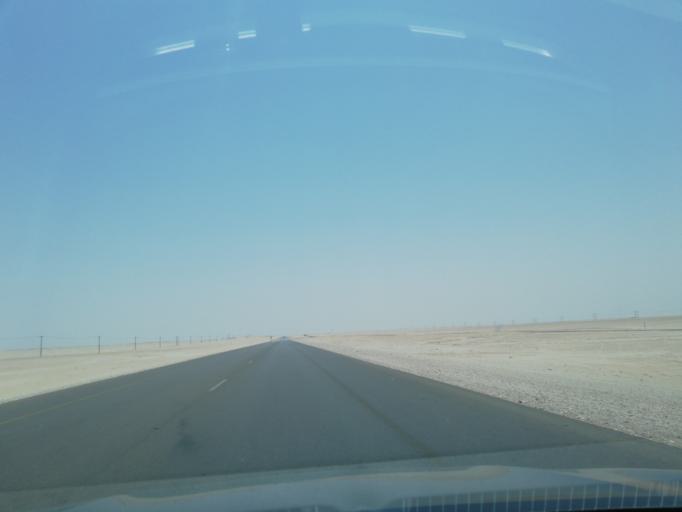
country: OM
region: Al Wusta
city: Hayma'
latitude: 19.8785
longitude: 56.1762
